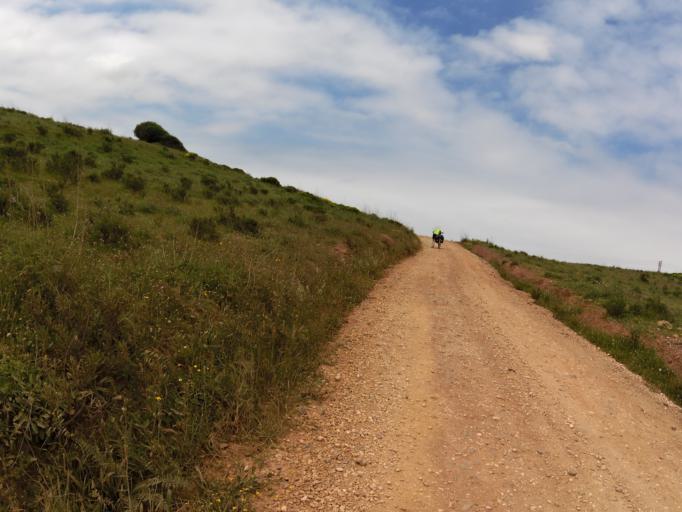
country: PT
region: Faro
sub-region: Vila do Bispo
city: Vila do Bispo
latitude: 37.0877
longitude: -8.8993
